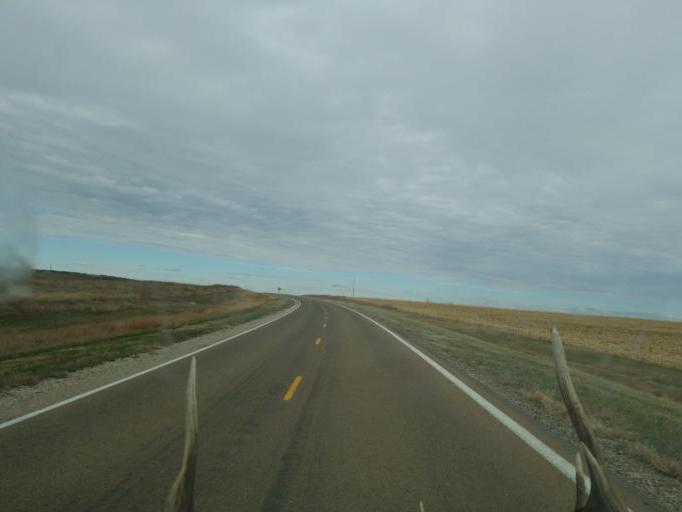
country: US
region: Kansas
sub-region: Logan County
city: Oakley
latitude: 39.0368
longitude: -101.2748
